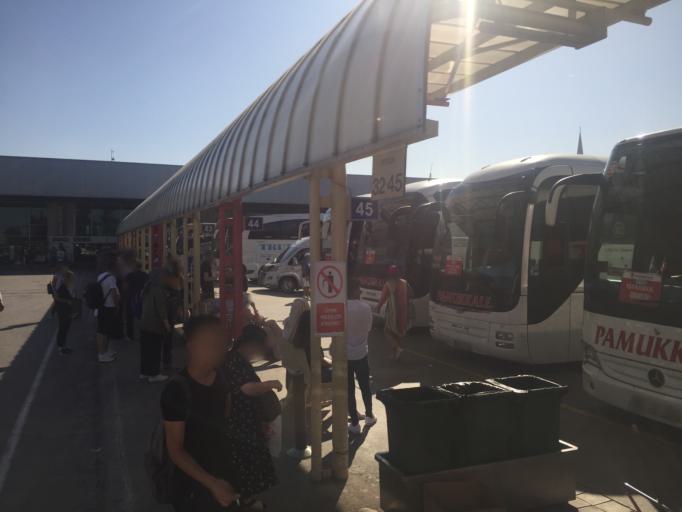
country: TR
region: Bursa
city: Demirtas
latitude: 40.2646
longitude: 29.0522
